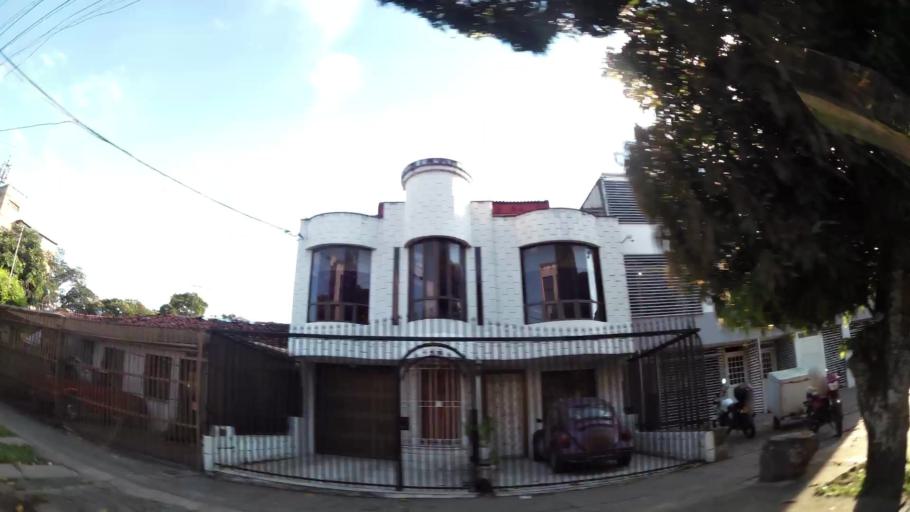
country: CO
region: Valle del Cauca
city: Cali
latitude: 3.4227
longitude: -76.5494
